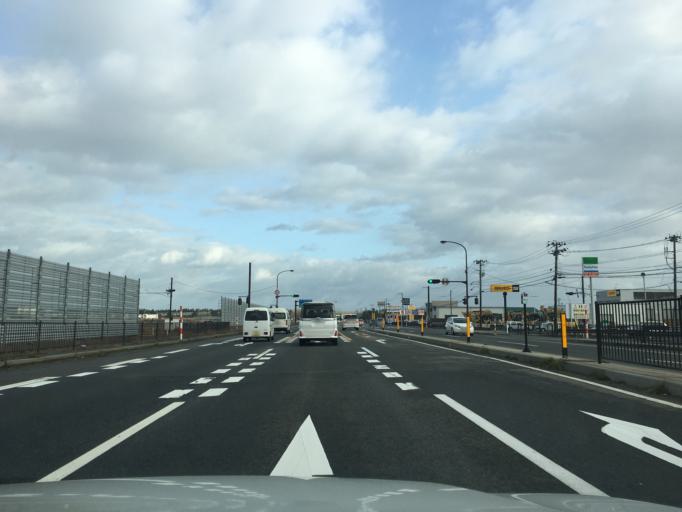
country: JP
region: Yamagata
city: Sakata
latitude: 38.8646
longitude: 139.8434
